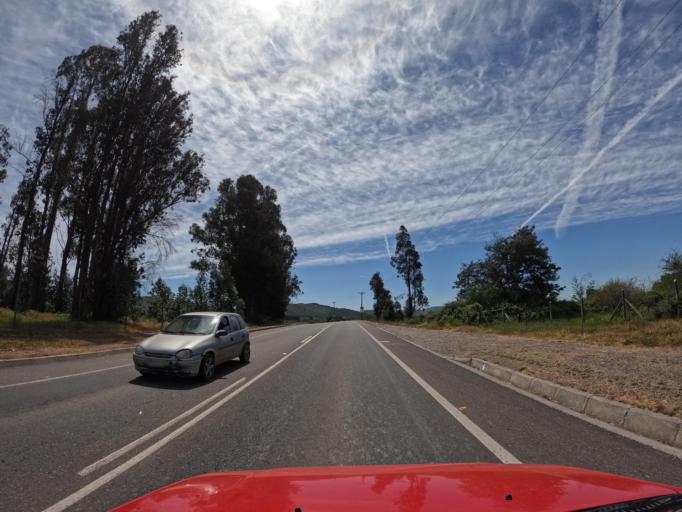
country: CL
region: Maule
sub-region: Provincia de Talca
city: Talca
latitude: -35.2832
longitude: -71.5308
